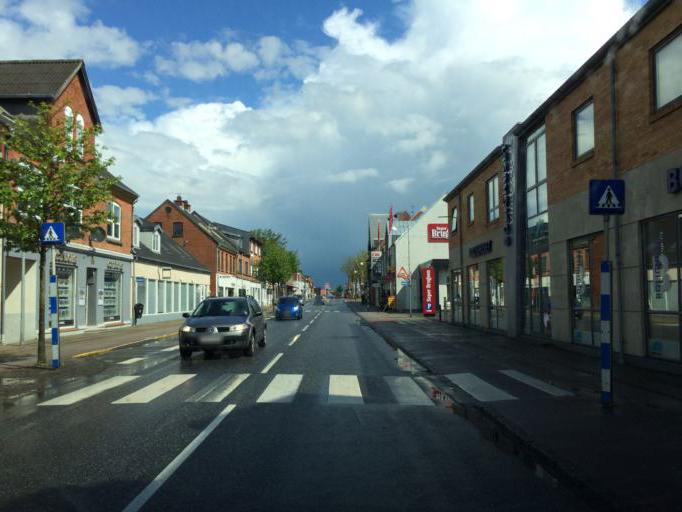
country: DK
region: Central Jutland
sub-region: Holstebro Kommune
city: Vinderup
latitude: 56.4805
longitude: 8.7786
